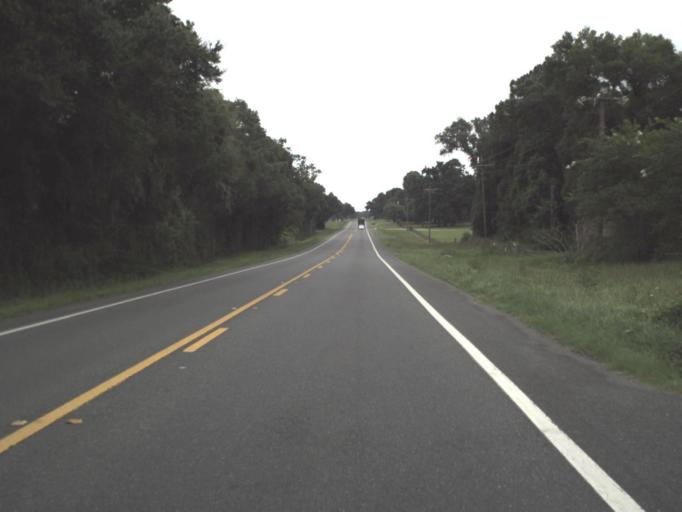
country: US
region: Florida
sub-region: Levy County
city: Williston
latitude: 29.3215
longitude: -82.4529
